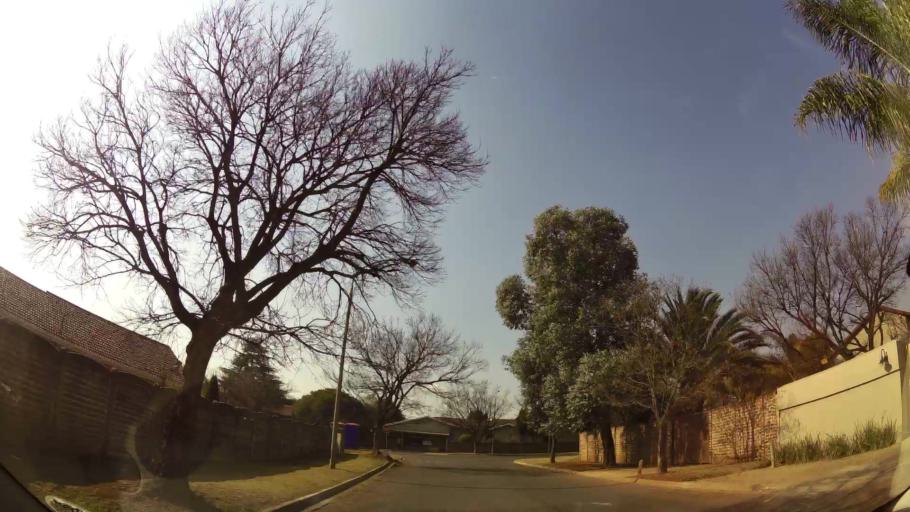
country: ZA
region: Gauteng
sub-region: Ekurhuleni Metropolitan Municipality
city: Benoni
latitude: -26.1548
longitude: 28.2909
